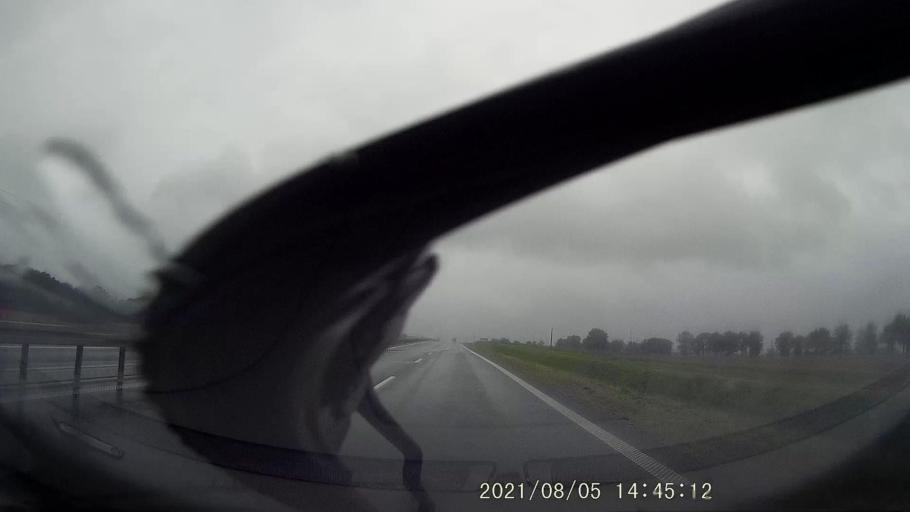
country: PL
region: Opole Voivodeship
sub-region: Powiat nyski
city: Nysa
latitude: 50.4985
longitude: 17.3640
